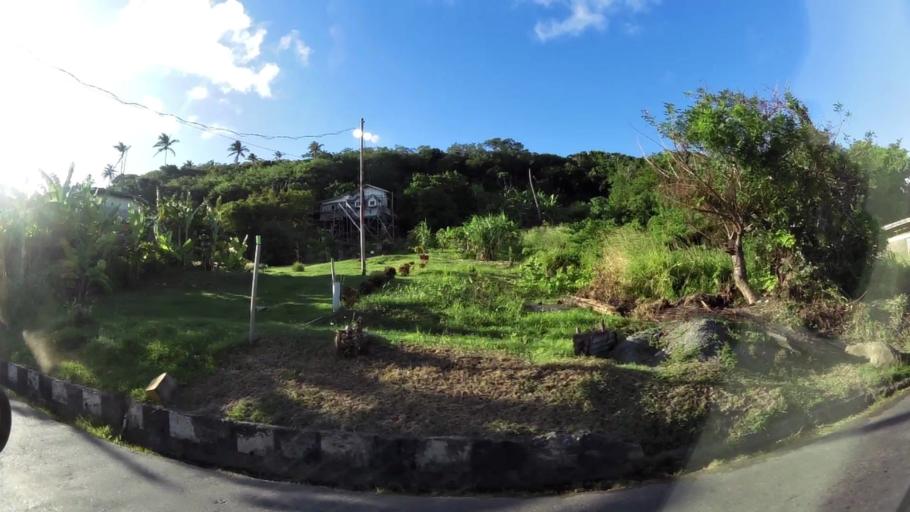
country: TT
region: Tobago
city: Scarborough
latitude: 11.1833
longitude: -60.6995
